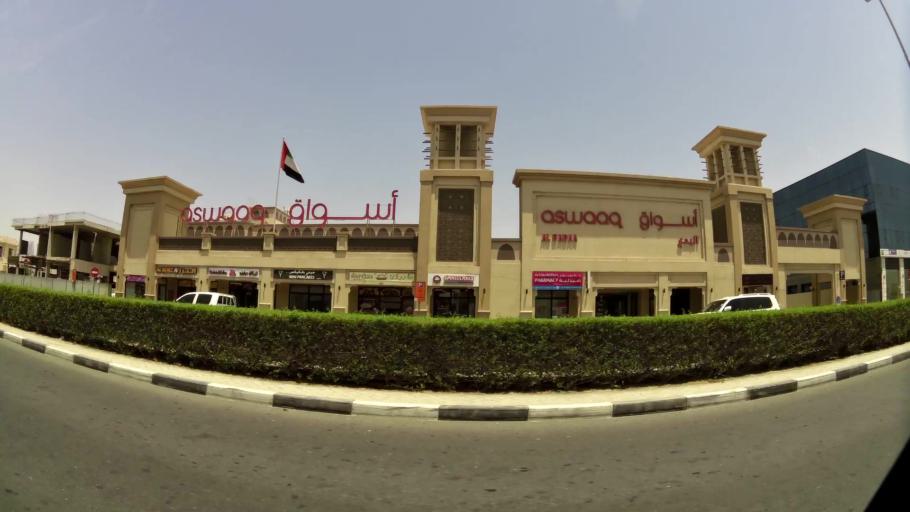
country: AE
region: Dubai
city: Dubai
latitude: 25.2142
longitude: 55.2585
